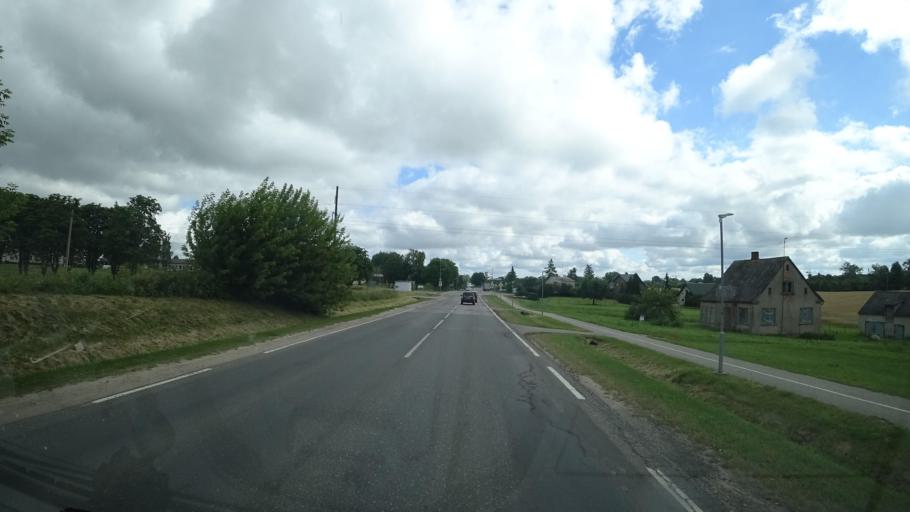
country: LT
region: Marijampoles apskritis
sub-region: Marijampole Municipality
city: Marijampole
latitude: 54.5328
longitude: 23.3337
